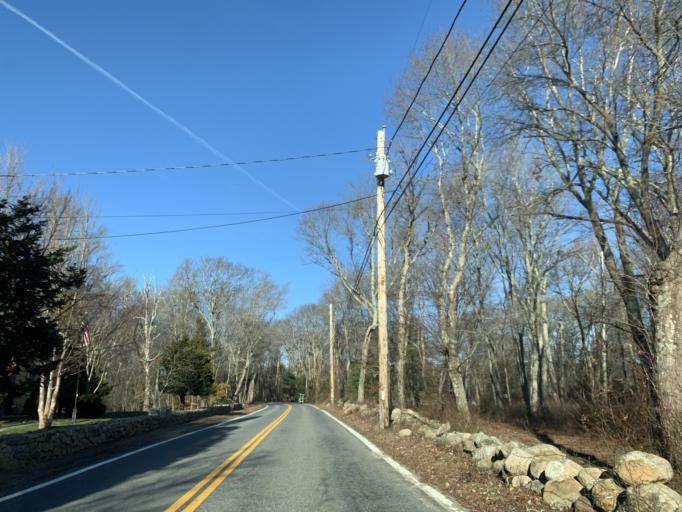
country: US
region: Rhode Island
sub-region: Washington County
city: Exeter
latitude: 41.5602
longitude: -71.5353
